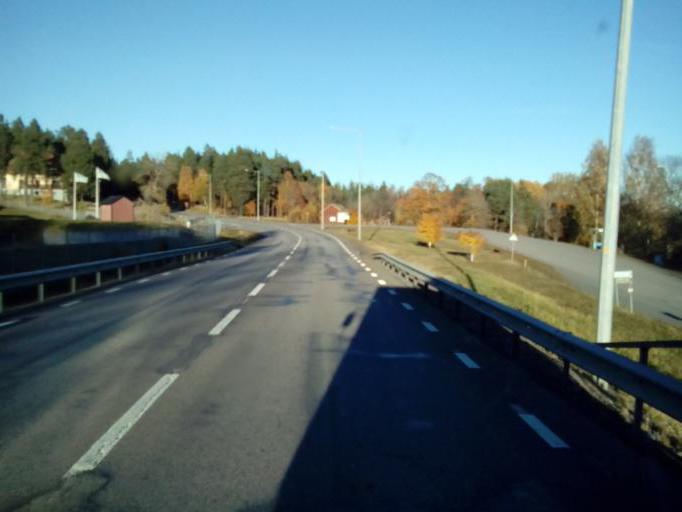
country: SE
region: OErebro
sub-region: Hallsbergs Kommun
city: Palsboda
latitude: 58.8971
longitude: 15.4327
